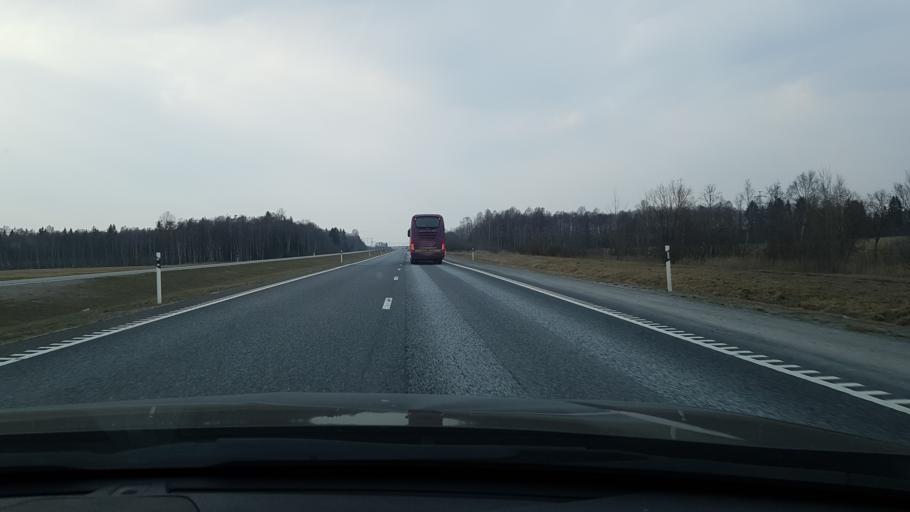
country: EE
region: Harju
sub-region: Rae vald
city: Vaida
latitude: 59.2641
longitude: 25.0003
